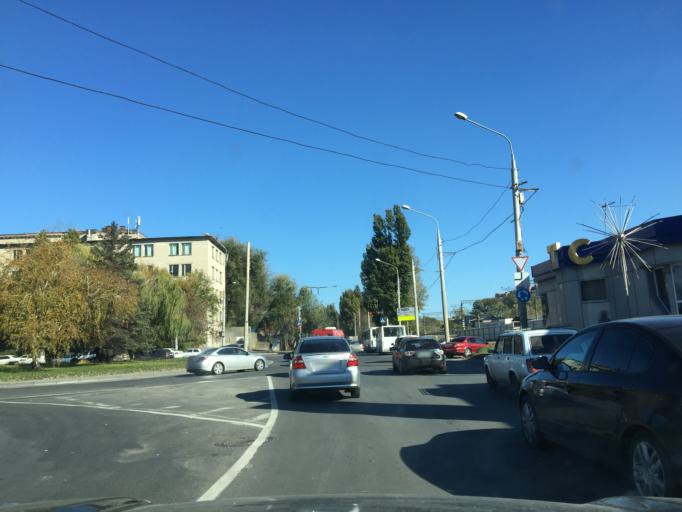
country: RU
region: Rostov
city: Imeni Chkalova
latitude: 47.2482
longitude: 39.7572
